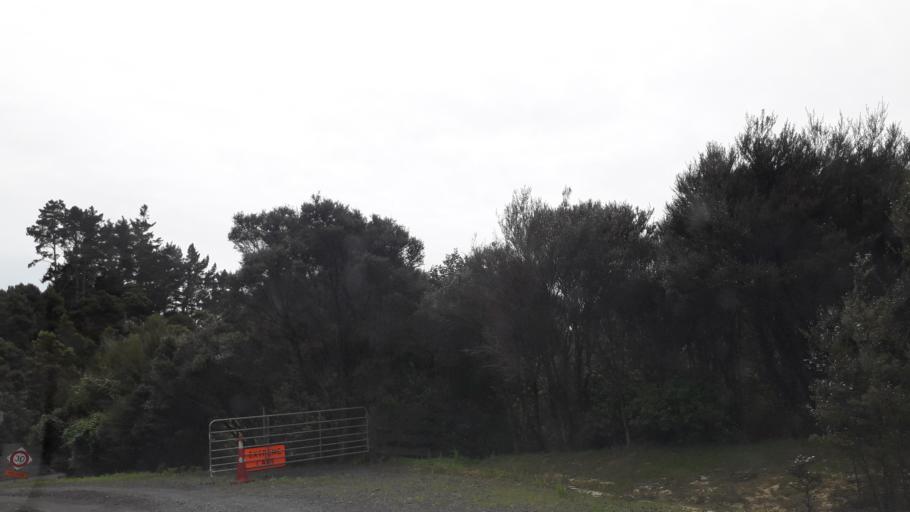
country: NZ
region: Northland
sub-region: Far North District
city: Paihia
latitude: -35.2800
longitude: 174.1833
